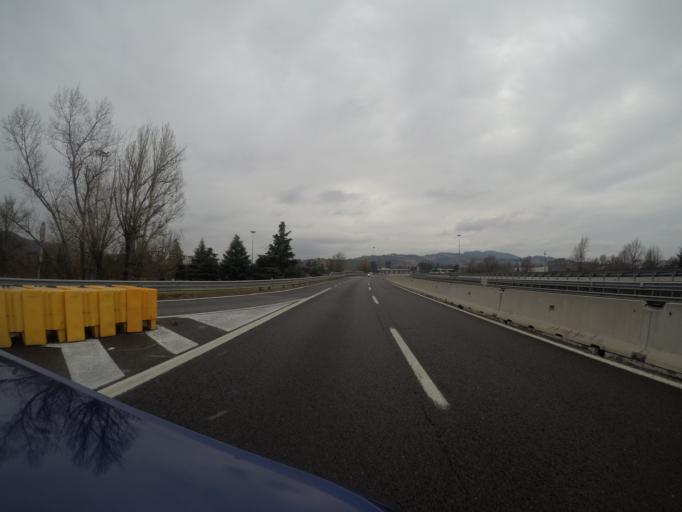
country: IT
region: Emilia-Romagna
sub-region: Provincia di Bologna
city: Casalecchio di Reno
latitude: 44.4912
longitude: 11.2704
